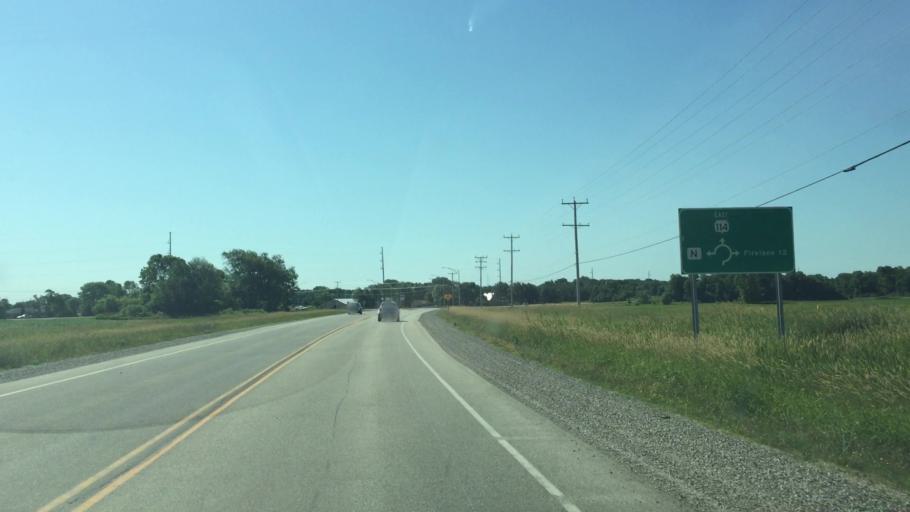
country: US
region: Wisconsin
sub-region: Outagamie County
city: Combined Locks
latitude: 44.2024
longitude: -88.3272
